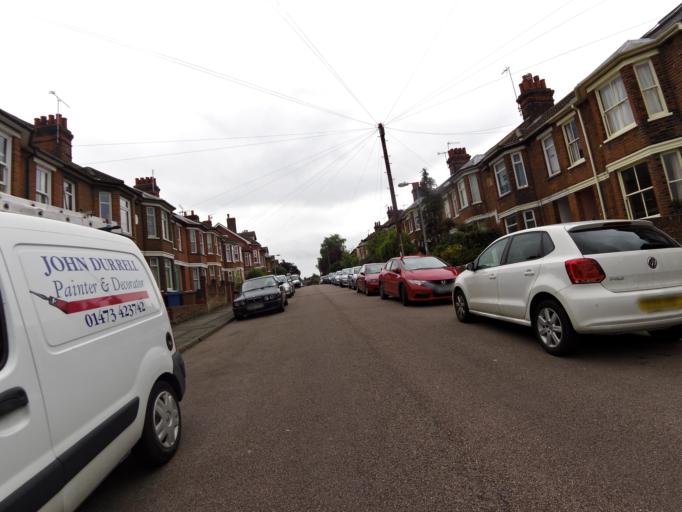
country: GB
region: England
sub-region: Suffolk
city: Ipswich
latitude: 52.0490
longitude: 1.1501
